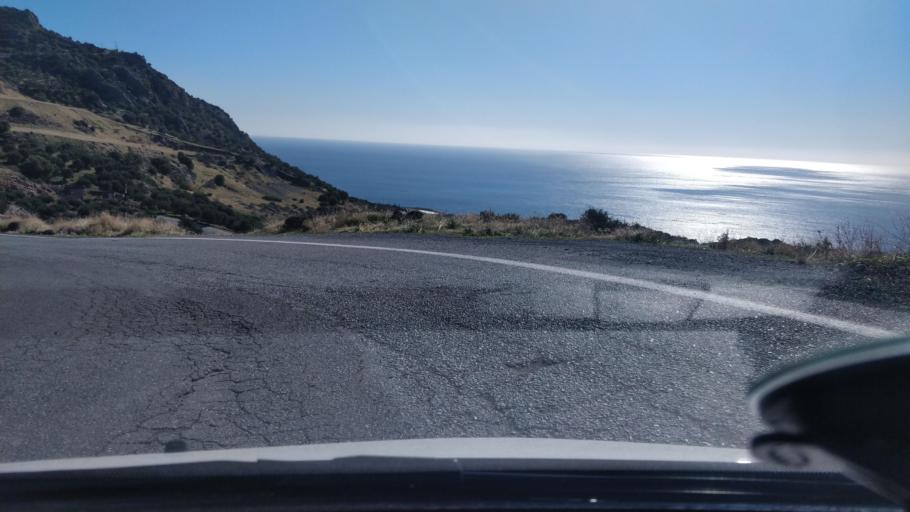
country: GR
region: Crete
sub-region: Nomos Irakleiou
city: Arkalochori
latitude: 35.0063
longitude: 25.4330
